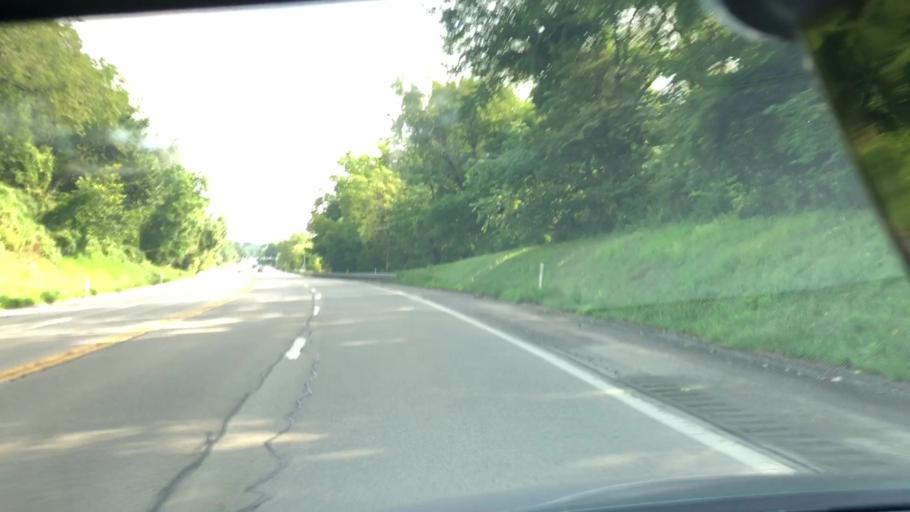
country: US
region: Pennsylvania
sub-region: Allegheny County
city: Bryn Mawr
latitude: 40.3092
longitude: -80.0914
